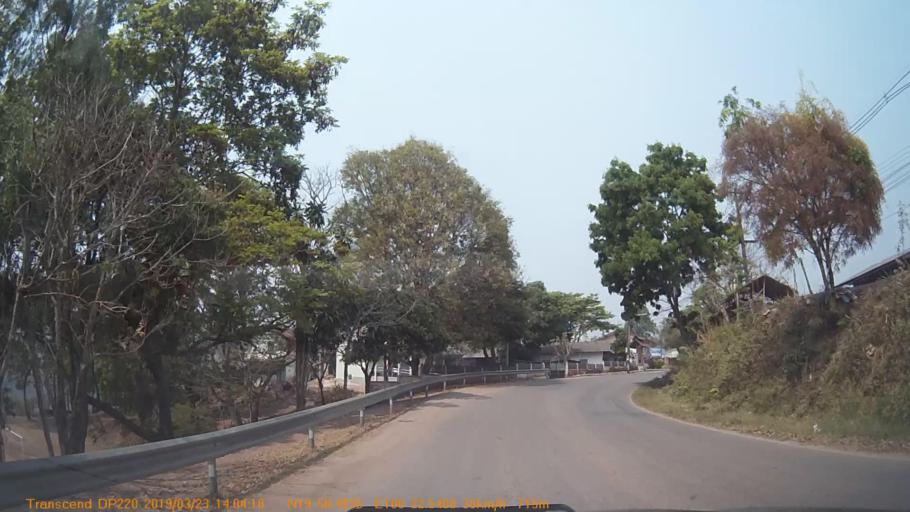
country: TH
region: Chiang Rai
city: Khun Tan
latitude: 19.8416
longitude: 100.3757
